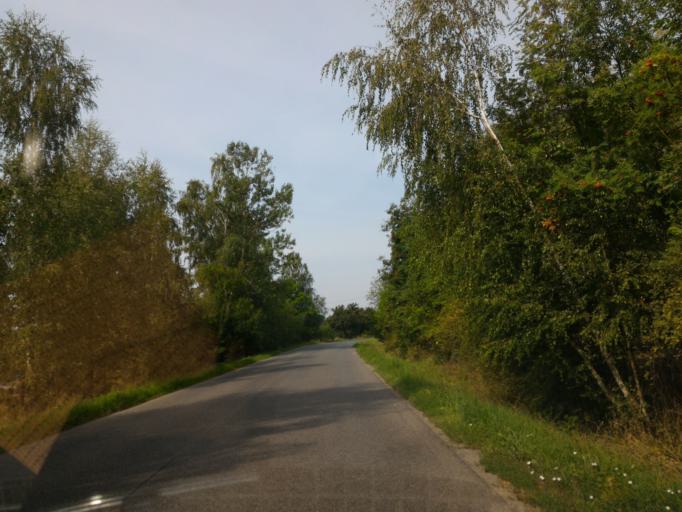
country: CZ
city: Prisovice
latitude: 50.5822
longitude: 15.1054
